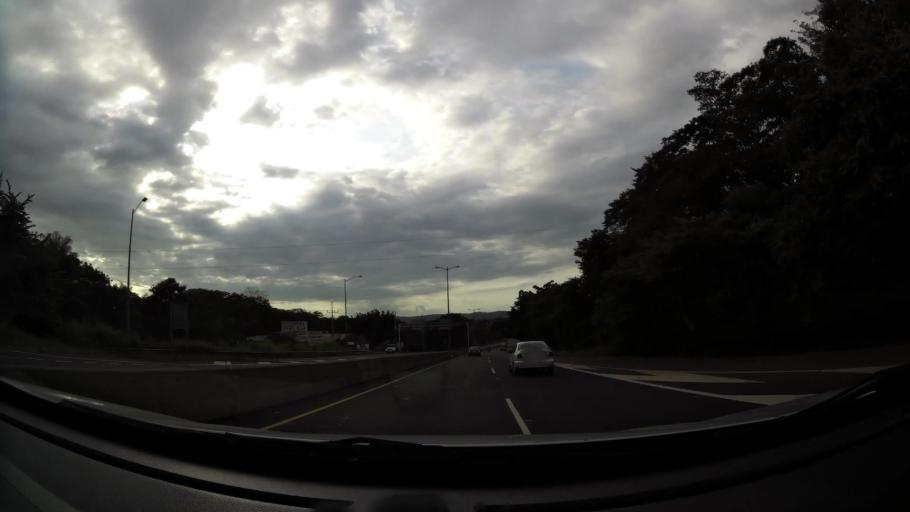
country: CR
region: Puntarenas
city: Esparza
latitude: 9.8919
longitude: -84.6460
